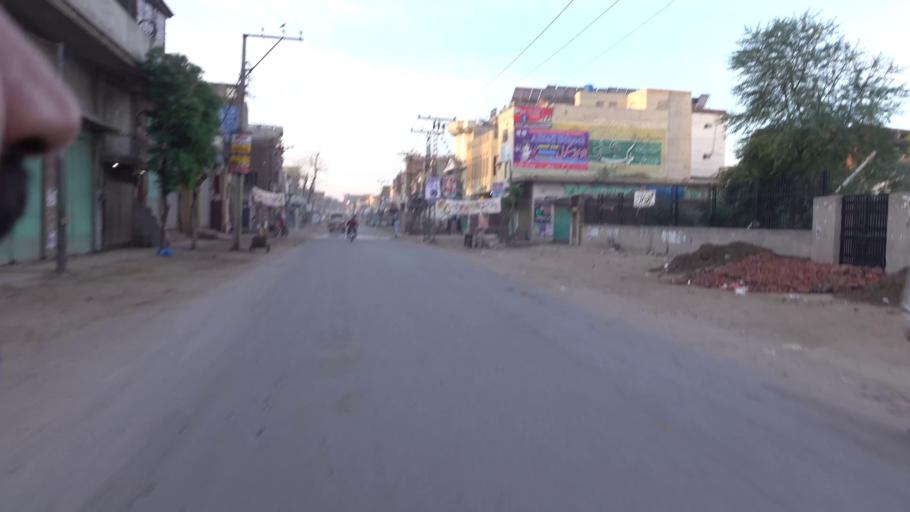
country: PK
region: Punjab
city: Hafizabad
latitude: 32.0689
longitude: 73.6890
